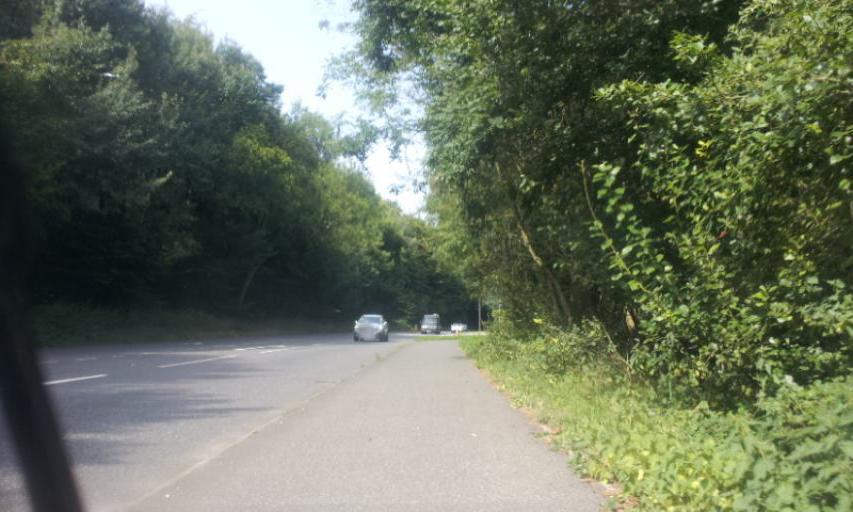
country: GB
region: England
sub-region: Kent
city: Boxley
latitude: 51.3289
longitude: 0.5197
